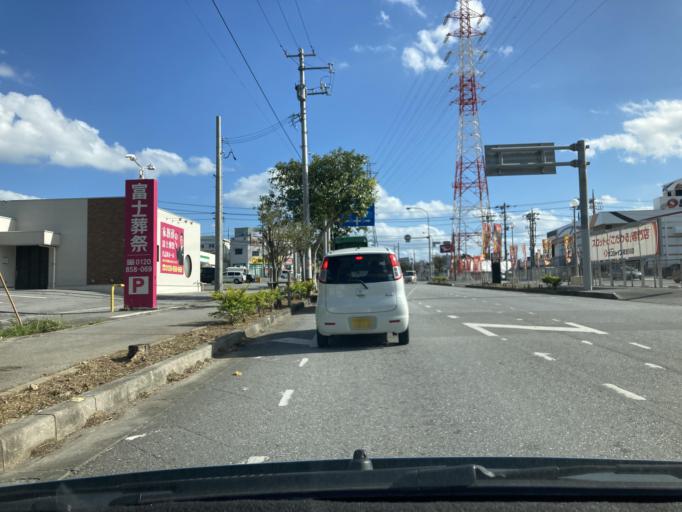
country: JP
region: Okinawa
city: Gushikawa
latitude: 26.3614
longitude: 127.8440
